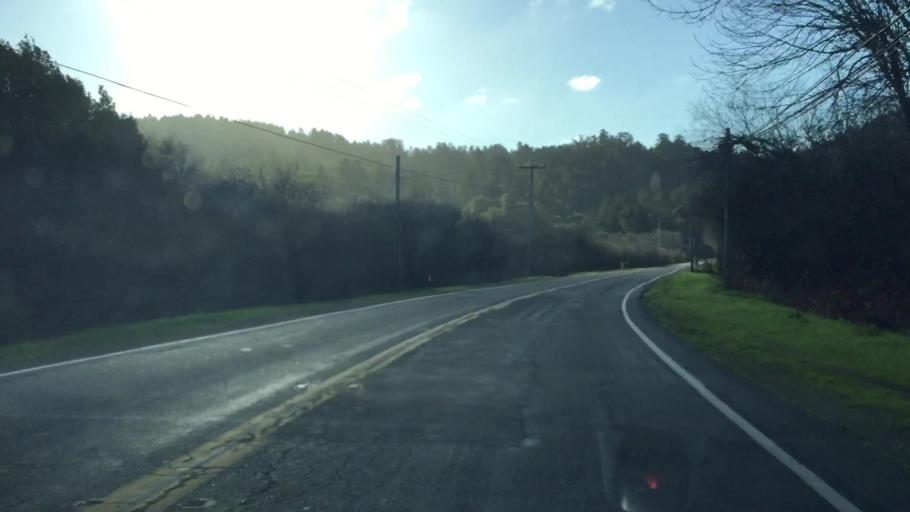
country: US
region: California
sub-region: Marin County
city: Inverness
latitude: 38.0634
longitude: -122.8115
